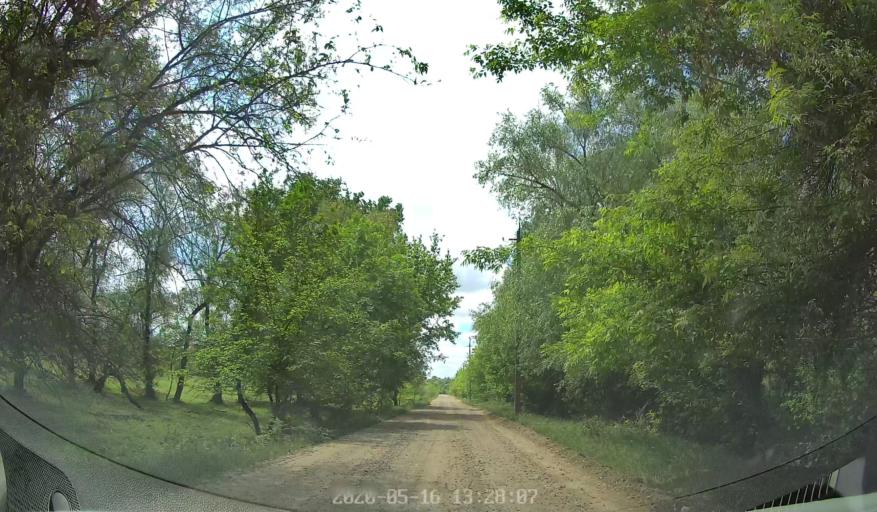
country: MD
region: Telenesti
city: Dnestrovsc
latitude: 46.5452
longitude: 29.9975
